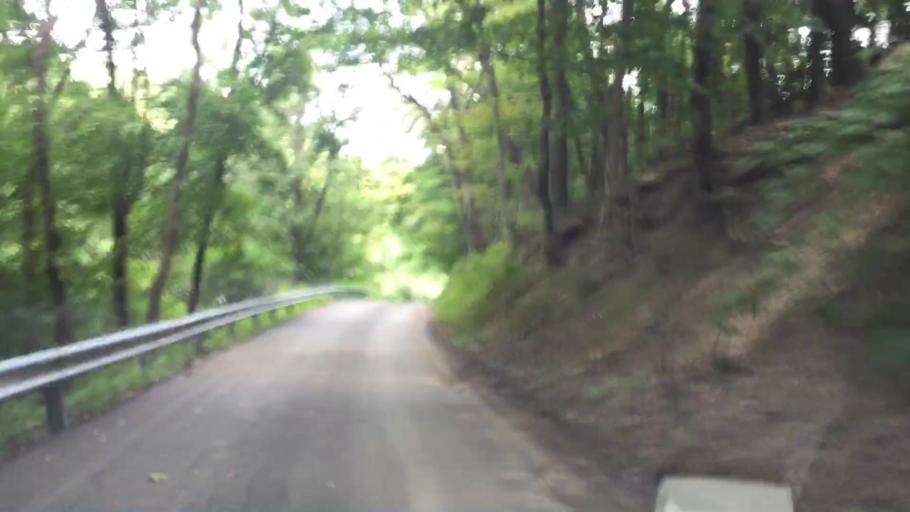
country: US
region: Pennsylvania
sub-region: Allegheny County
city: Millvale
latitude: 40.5039
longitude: -79.9981
